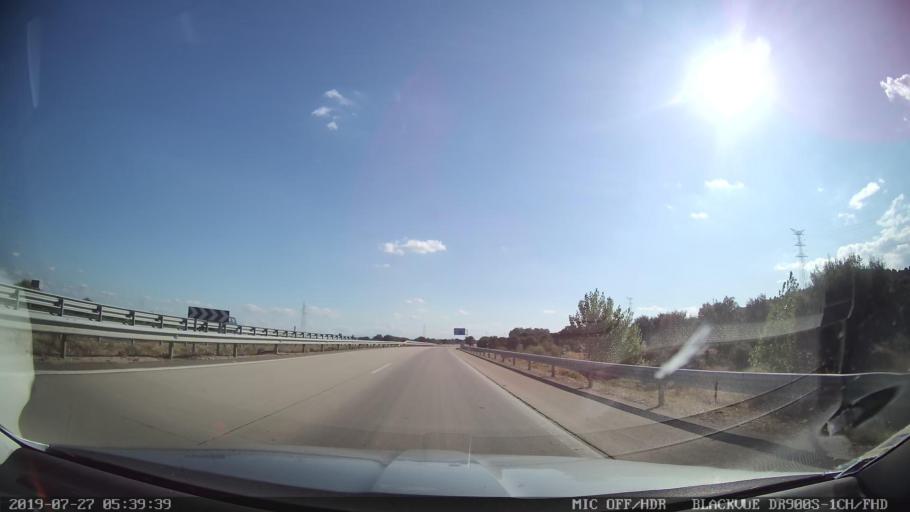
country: ES
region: Castille-La Mancha
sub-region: Province of Toledo
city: Talavera de la Reina
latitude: 39.9897
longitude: -4.8399
